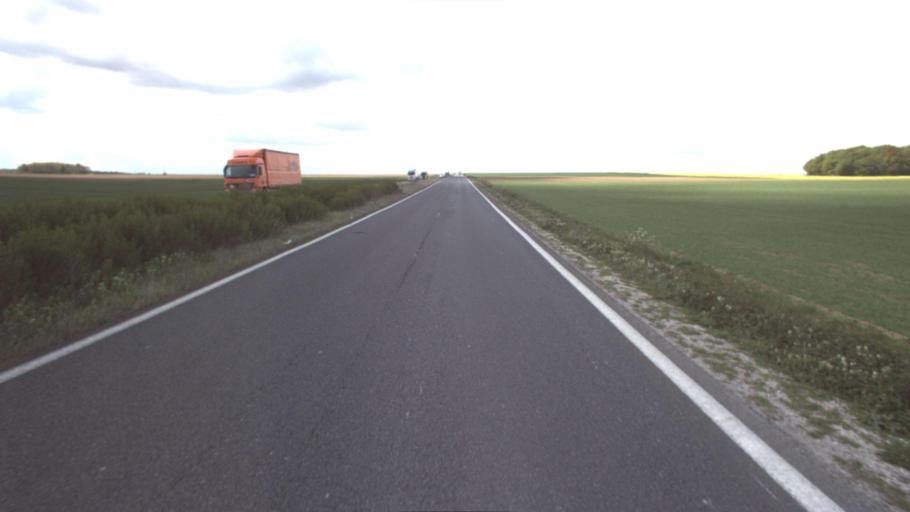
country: FR
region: Ile-de-France
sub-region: Departement de Seine-et-Marne
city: Jouy-le-Chatel
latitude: 48.6849
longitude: 3.0632
